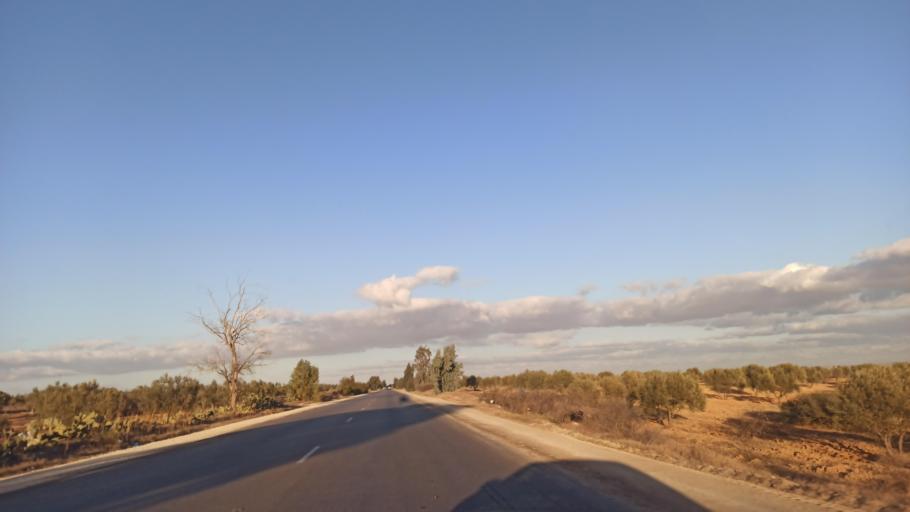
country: TN
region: Al Qayrawan
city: Sbikha
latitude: 35.8648
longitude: 10.2106
